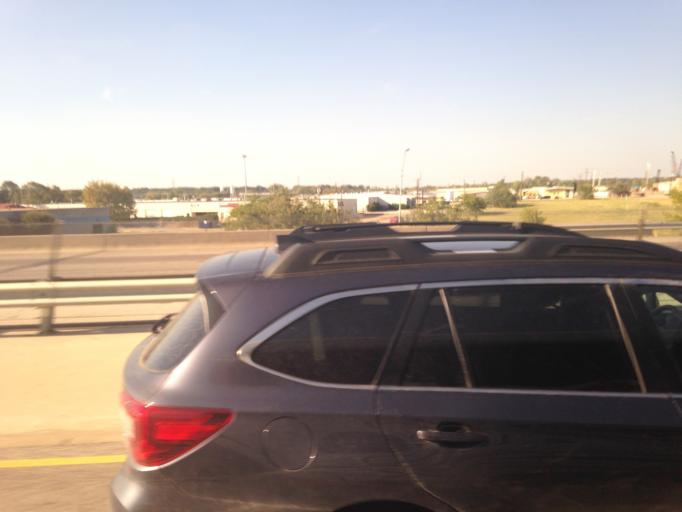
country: US
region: Texas
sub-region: Tarrant County
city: Haltom City
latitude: 32.7919
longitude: -97.2448
